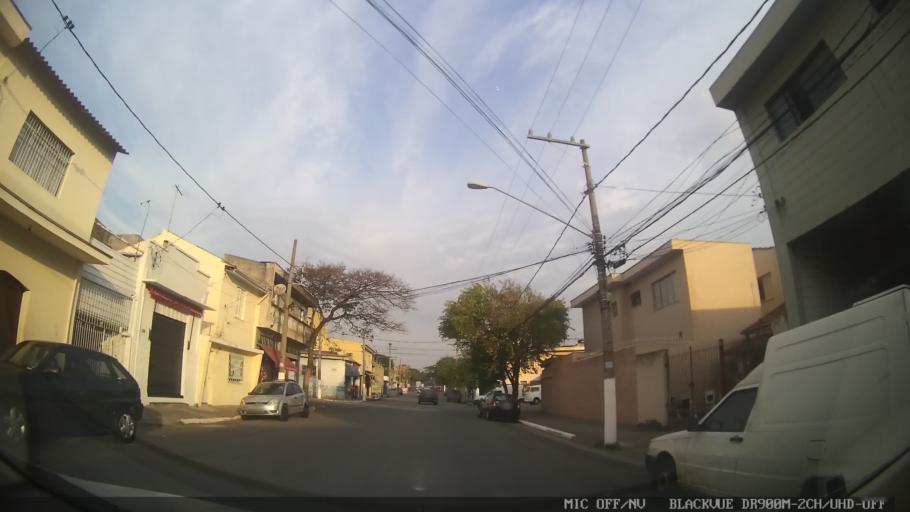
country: BR
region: Sao Paulo
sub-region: Sao Caetano Do Sul
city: Sao Caetano do Sul
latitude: -23.6011
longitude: -46.5928
